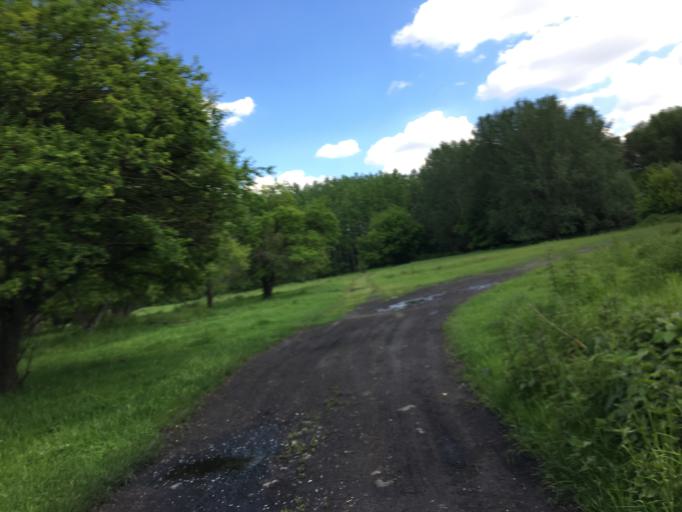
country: HU
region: Pest
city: Urom
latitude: 47.5757
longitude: 19.0407
